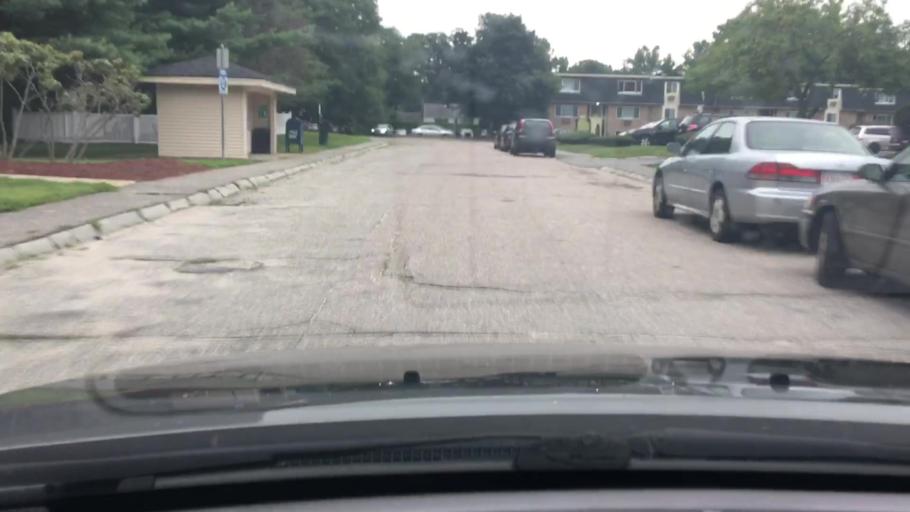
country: US
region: Massachusetts
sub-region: Worcester County
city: Hopedale
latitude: 42.1572
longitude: -71.5373
